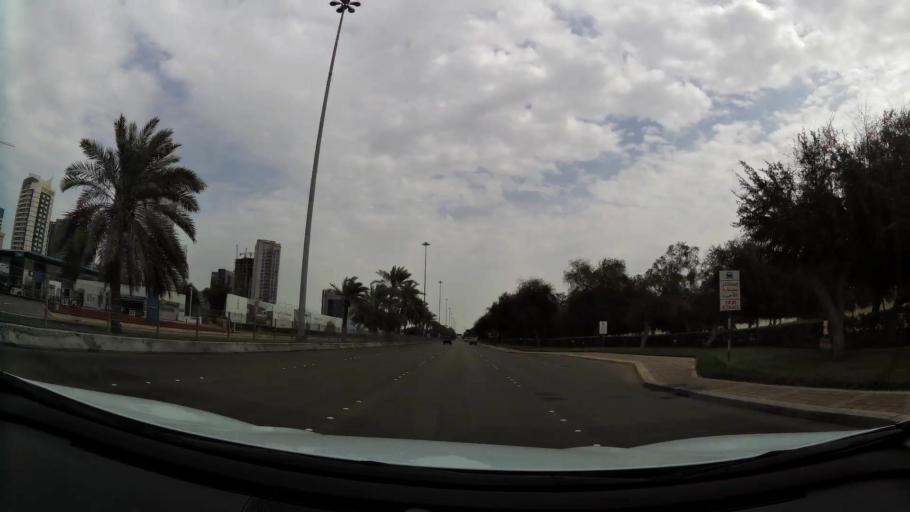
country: AE
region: Abu Dhabi
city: Abu Dhabi
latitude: 24.4281
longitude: 54.4318
